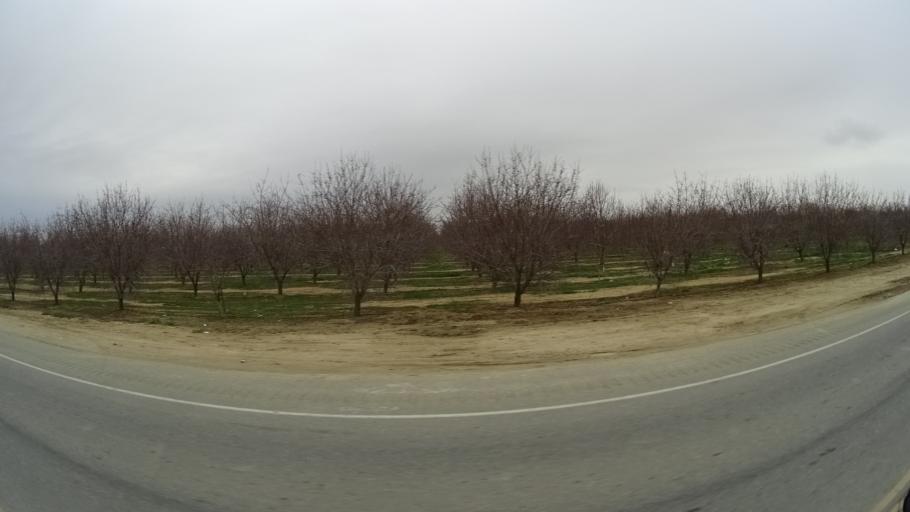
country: US
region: California
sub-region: Kern County
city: Lamont
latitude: 35.3192
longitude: -118.9321
